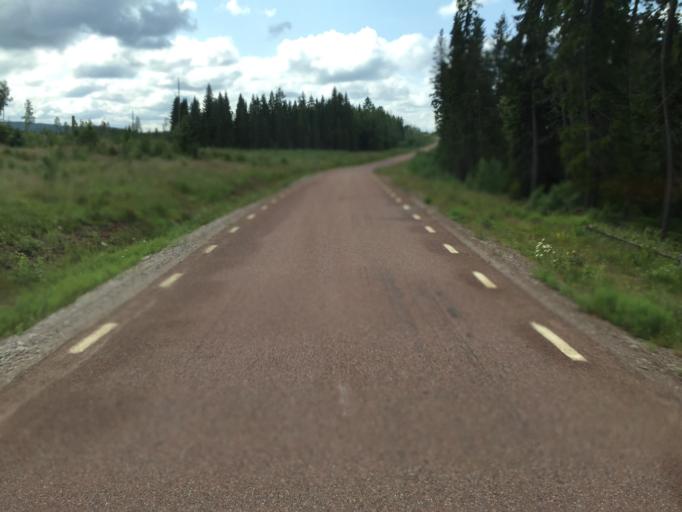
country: SE
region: Dalarna
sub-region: Malung-Saelens kommun
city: Malung
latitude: 60.4397
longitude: 13.8928
